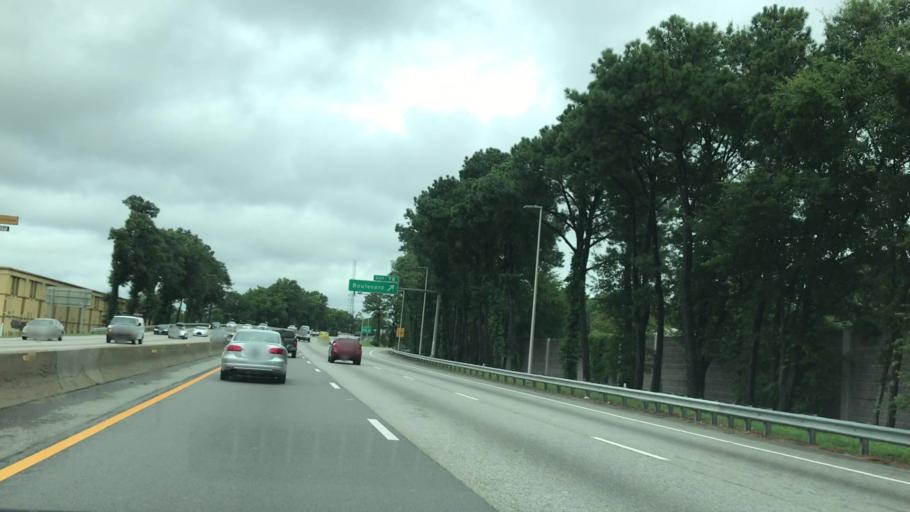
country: US
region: Virginia
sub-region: City of Richmond
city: Richmond
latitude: 37.5732
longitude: -77.4584
